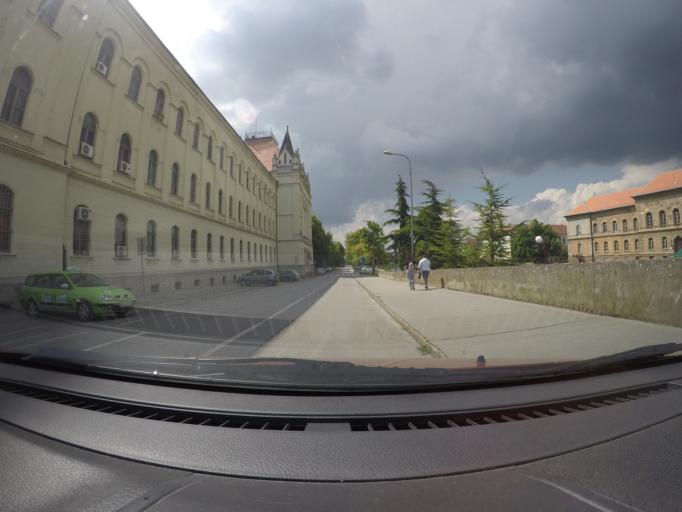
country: RS
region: Autonomna Pokrajina Vojvodina
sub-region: Srednjebanatski Okrug
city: Zrenjanin
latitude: 45.3789
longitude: 20.3891
